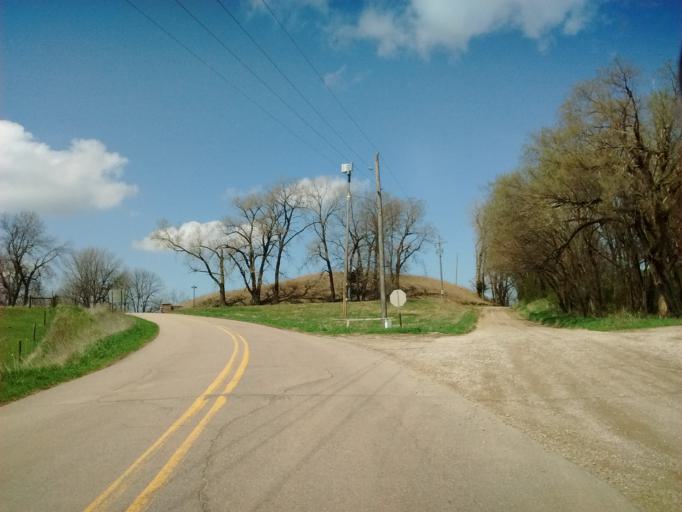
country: US
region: South Dakota
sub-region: Union County
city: North Sioux City
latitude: 42.5524
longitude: -96.4573
